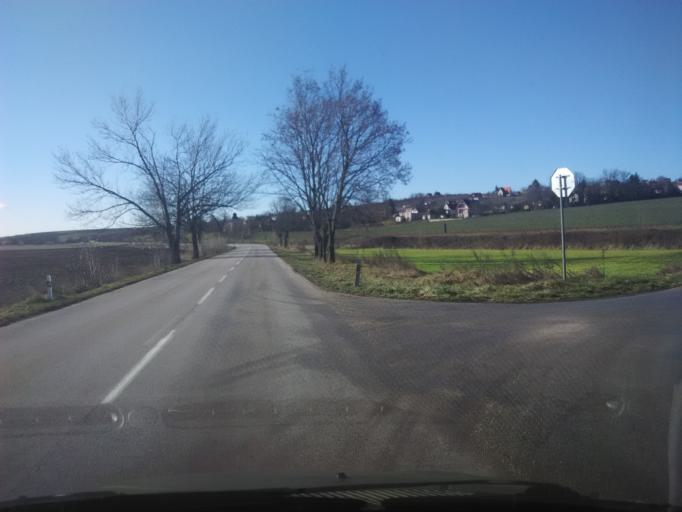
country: SK
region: Nitriansky
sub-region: Okres Nitra
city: Vrable
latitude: 48.2493
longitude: 18.2927
